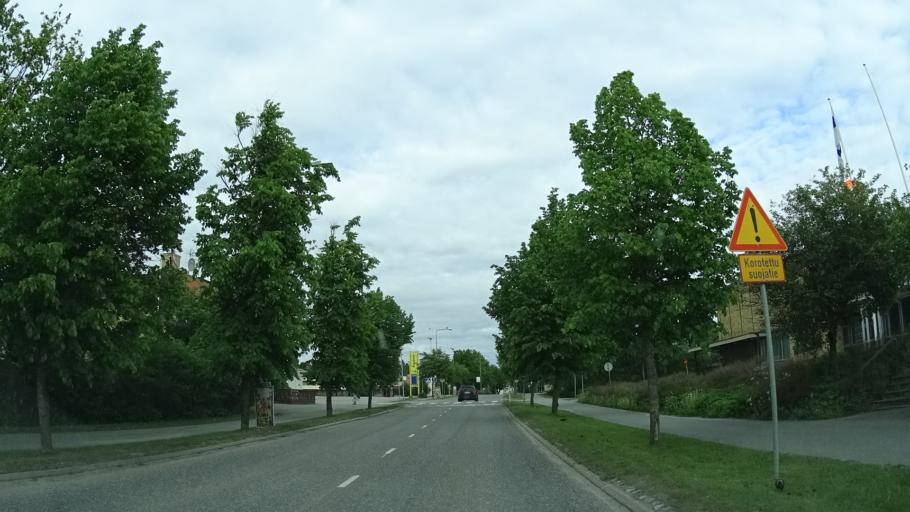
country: FI
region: Paijanne Tavastia
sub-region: Lahti
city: Sysmae
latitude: 61.5021
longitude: 25.6865
